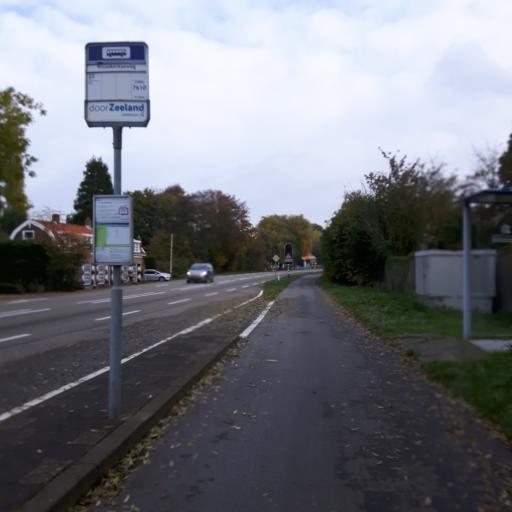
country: NL
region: Zeeland
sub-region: Gemeente Goes
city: Goes
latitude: 51.5014
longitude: 3.8458
